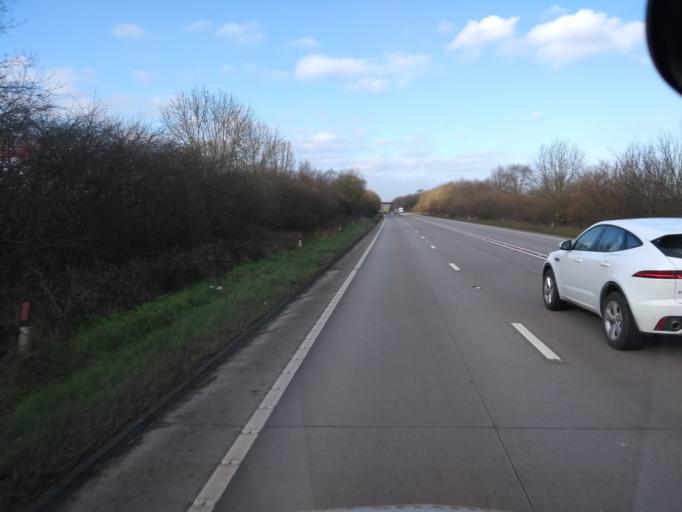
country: GB
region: England
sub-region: Somerset
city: Ilminster
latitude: 50.9386
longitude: -2.8800
